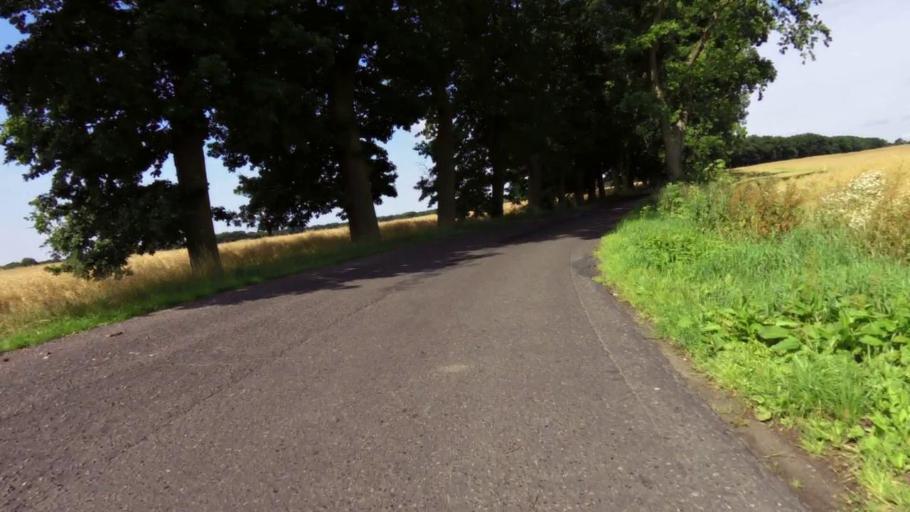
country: PL
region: West Pomeranian Voivodeship
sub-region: Powiat stargardzki
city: Stara Dabrowa
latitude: 53.3411
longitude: 15.1727
